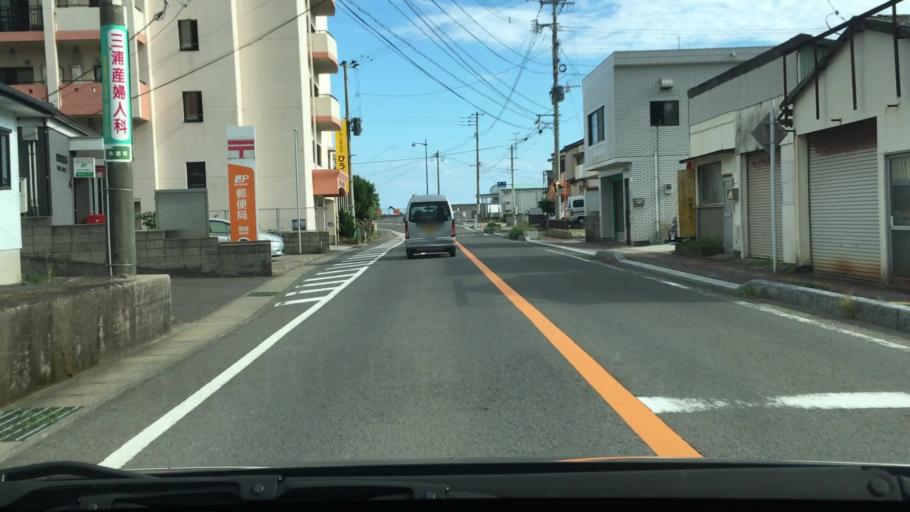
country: JP
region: Nagasaki
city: Togitsu
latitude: 32.8366
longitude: 129.7141
